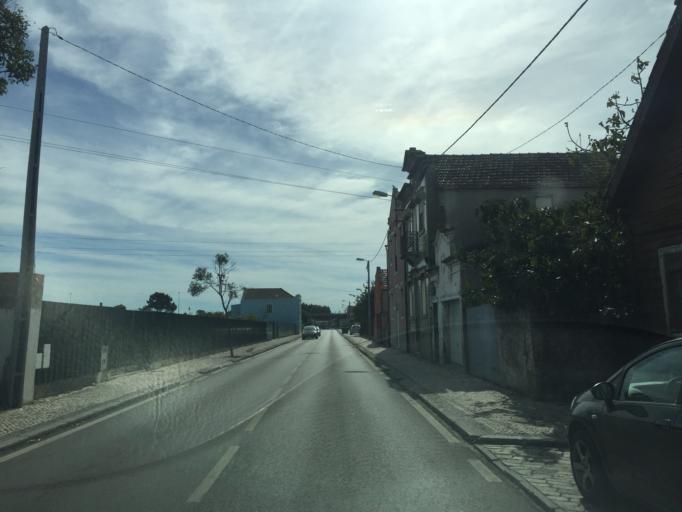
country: PT
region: Coimbra
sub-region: Figueira da Foz
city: Figueira da Foz
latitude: 40.1257
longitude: -8.8519
